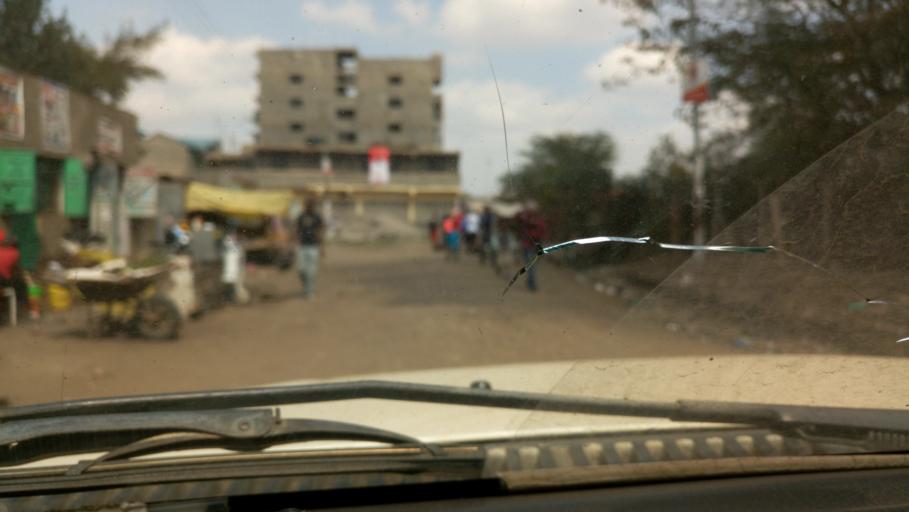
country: KE
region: Nairobi Area
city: Pumwani
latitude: -1.2668
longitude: 36.8867
